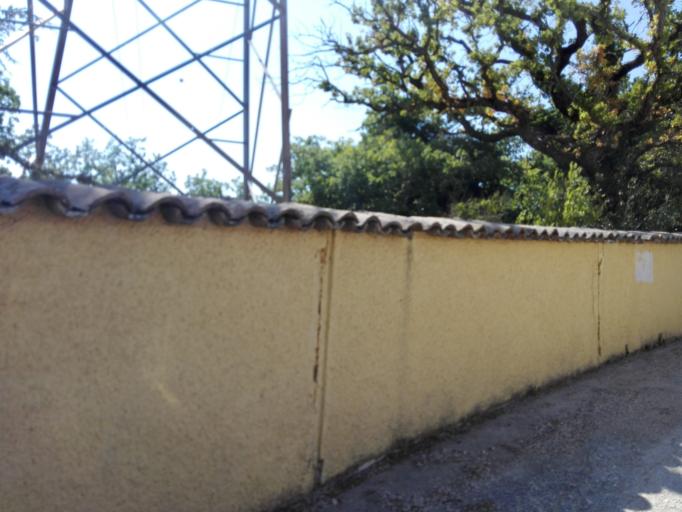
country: IT
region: Umbria
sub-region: Provincia di Perugia
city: Foligno
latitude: 42.9767
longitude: 12.7102
